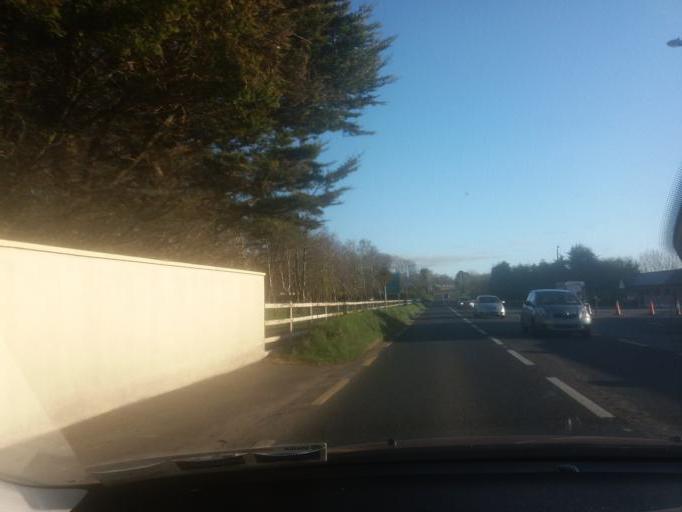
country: IE
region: Munster
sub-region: Ciarrai
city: Killorglin
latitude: 52.1622
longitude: -9.7028
